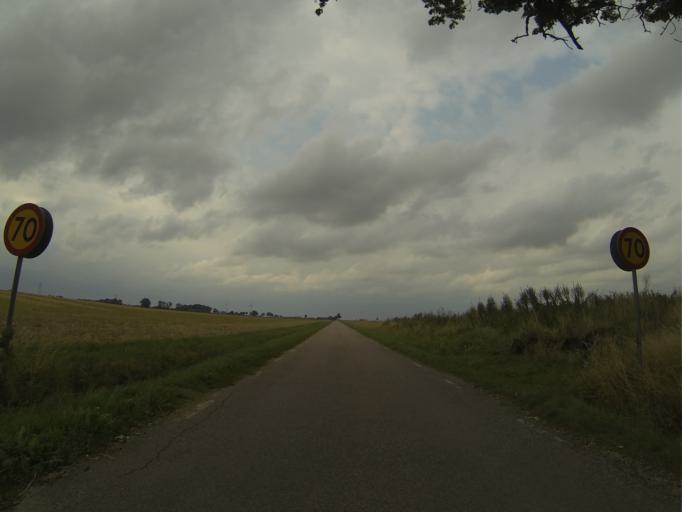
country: SE
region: Skane
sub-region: Kavlinge Kommun
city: Kaevlinge
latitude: 55.7662
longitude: 13.1673
